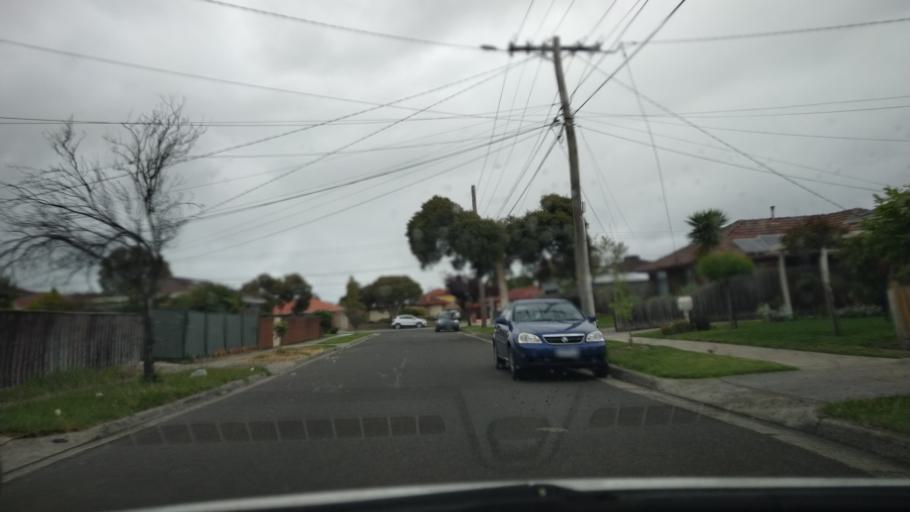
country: AU
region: Victoria
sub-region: Greater Dandenong
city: Keysborough
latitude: -37.9831
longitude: 145.1714
